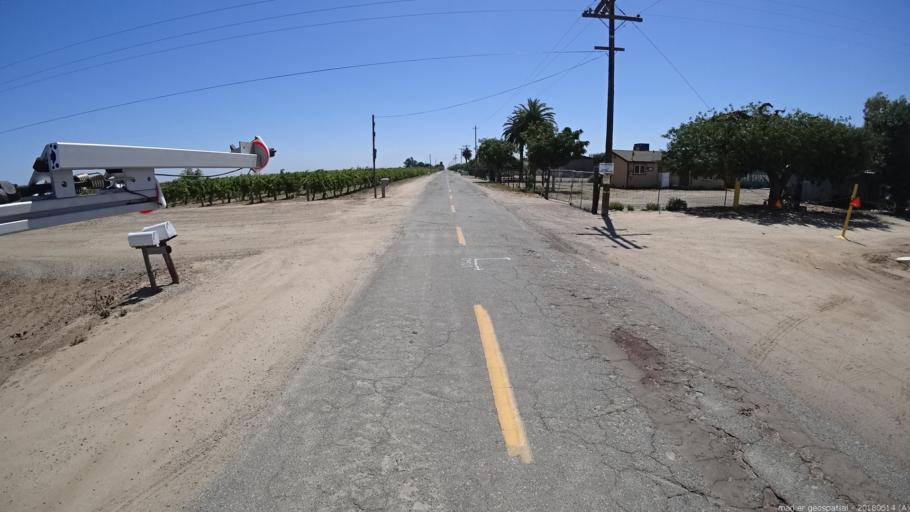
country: US
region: California
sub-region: Madera County
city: Fairmead
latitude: 36.9892
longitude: -120.2115
